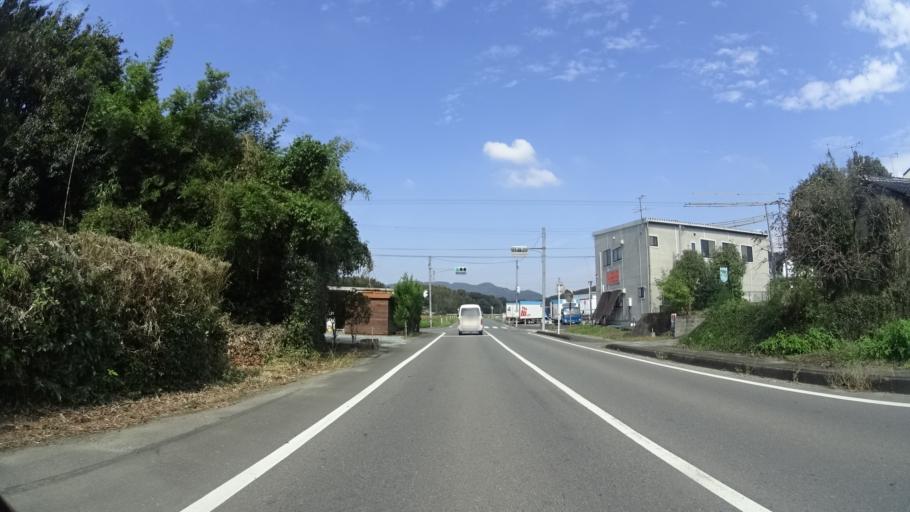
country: JP
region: Kumamoto
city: Matsubase
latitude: 32.6520
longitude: 130.7161
